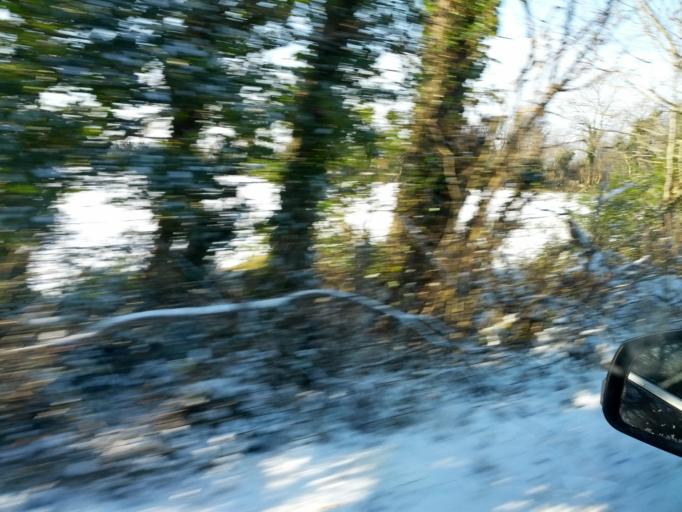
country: IE
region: Connaught
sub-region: County Galway
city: Athenry
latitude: 53.1797
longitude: -8.7330
